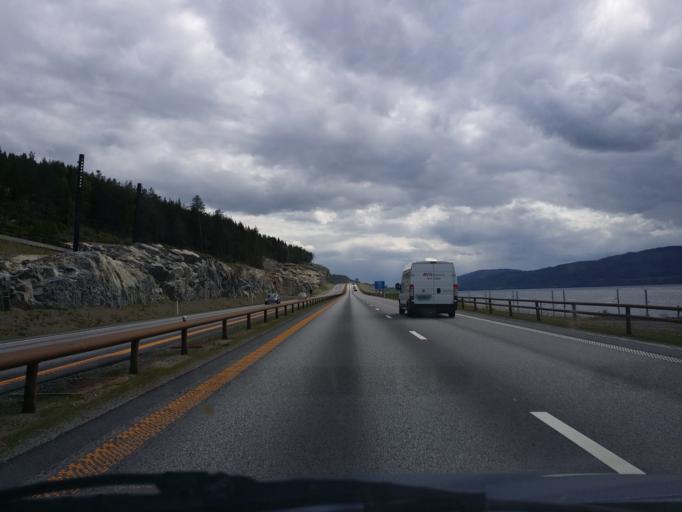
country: NO
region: Hedmark
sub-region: Stange
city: Stange
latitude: 60.5294
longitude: 11.2433
